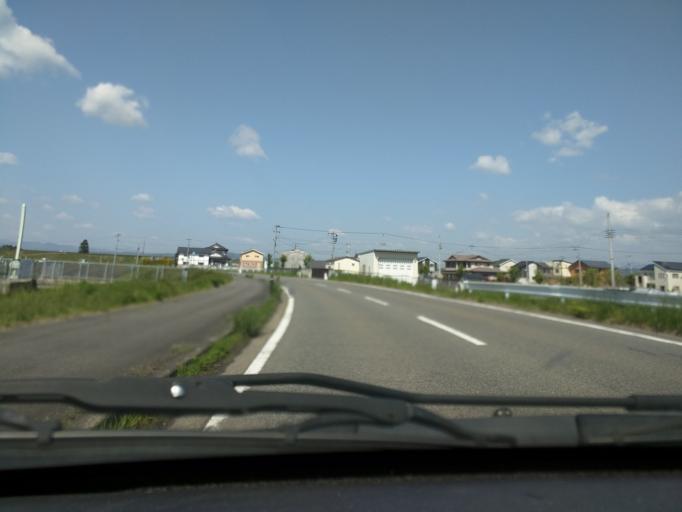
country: JP
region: Fukushima
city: Kitakata
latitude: 37.5947
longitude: 139.8813
